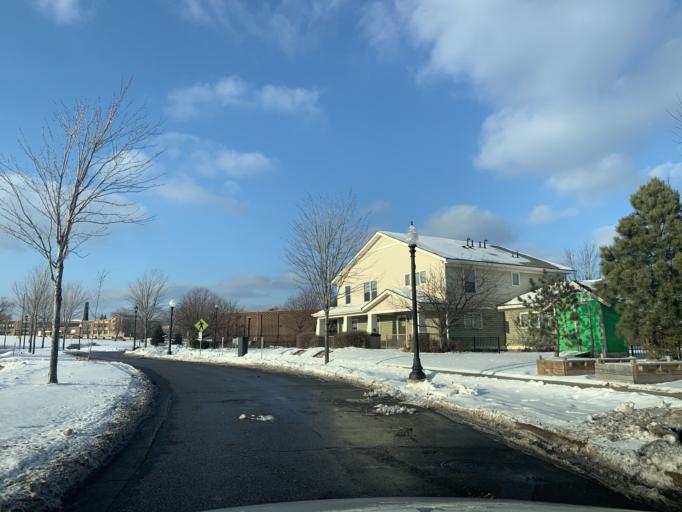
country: US
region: Minnesota
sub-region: Hennepin County
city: Minneapolis
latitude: 44.9828
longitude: -93.2931
